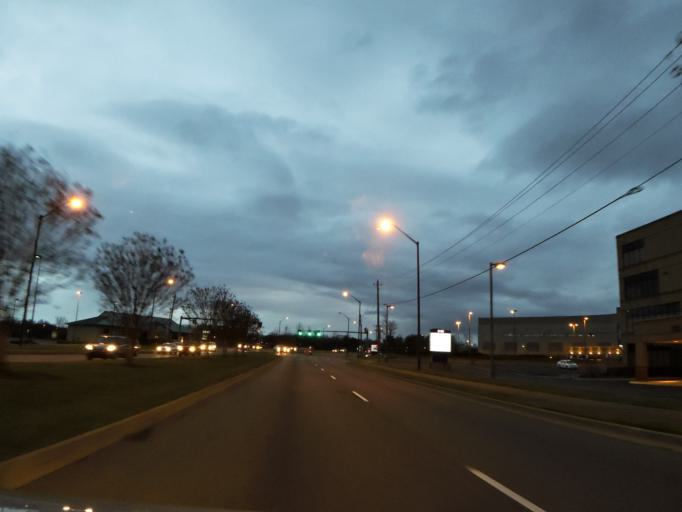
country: US
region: Tennessee
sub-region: Washington County
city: Johnson City
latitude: 36.3047
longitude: -82.3846
